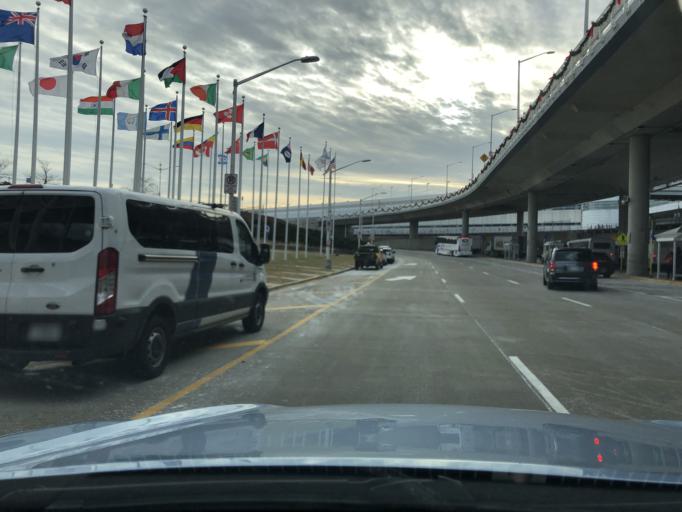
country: US
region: Illinois
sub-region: Cook County
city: Rosemont
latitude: 41.9752
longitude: -87.8899
